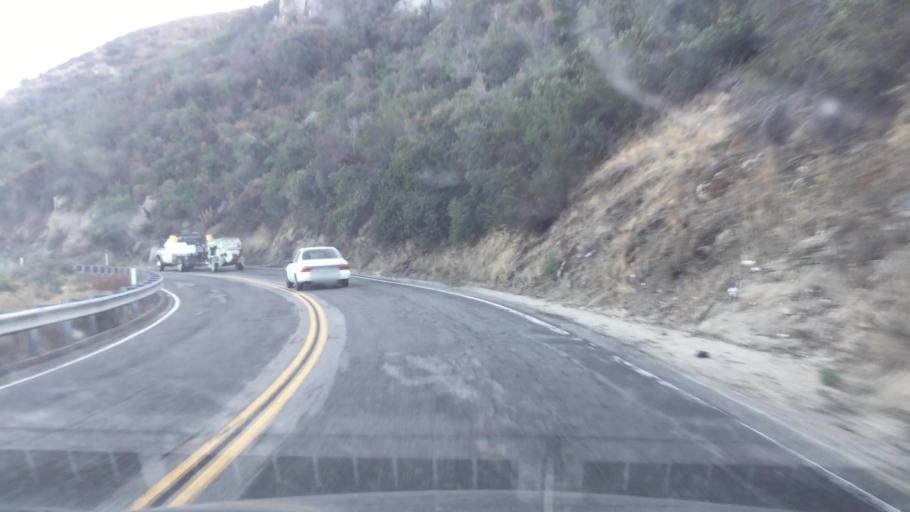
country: US
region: California
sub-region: Riverside County
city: Lakeland Village
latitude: 33.6500
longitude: -117.3902
